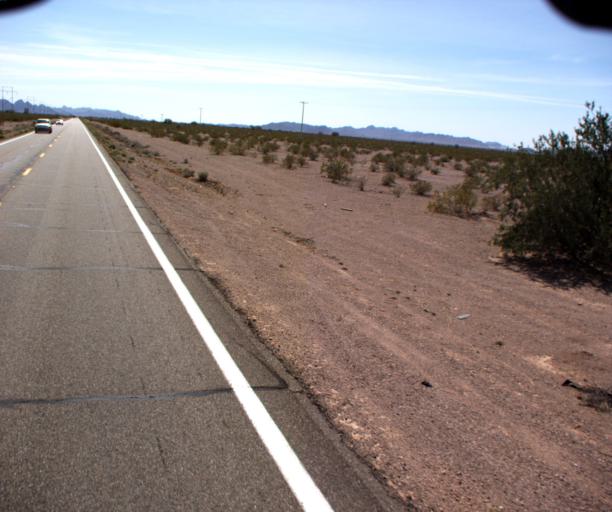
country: US
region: Arizona
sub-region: La Paz County
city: Quartzsite
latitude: 33.4235
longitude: -114.2170
